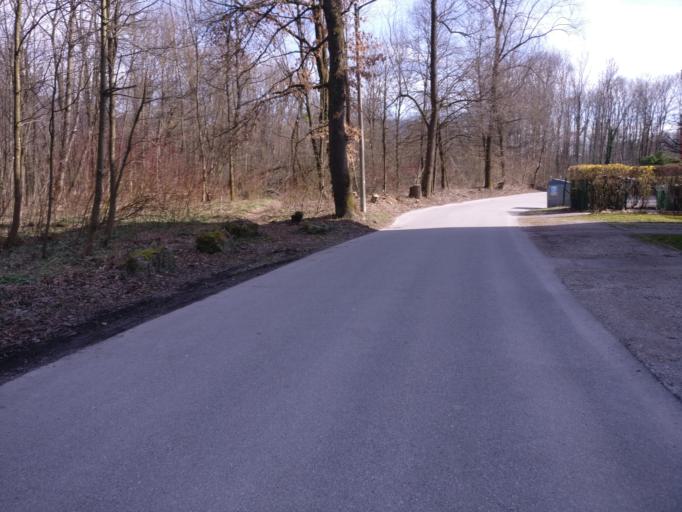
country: AT
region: Salzburg
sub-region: Salzburg Stadt
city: Salzburg
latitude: 47.7828
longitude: 13.0729
